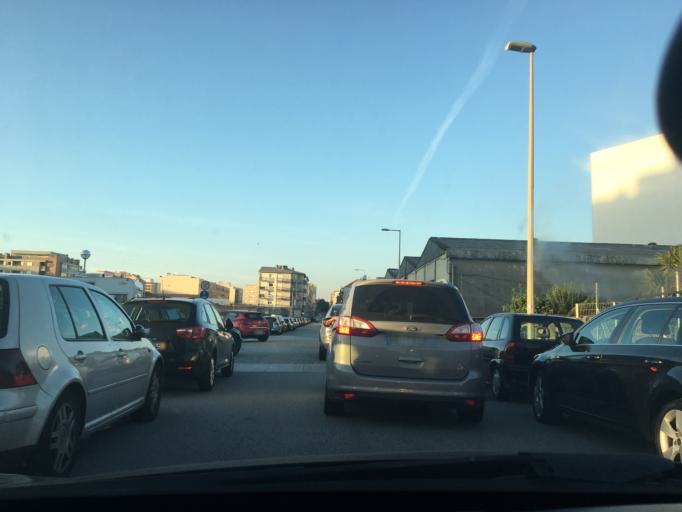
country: PT
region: Porto
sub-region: Matosinhos
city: Matosinhos
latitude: 41.1751
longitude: -8.6870
